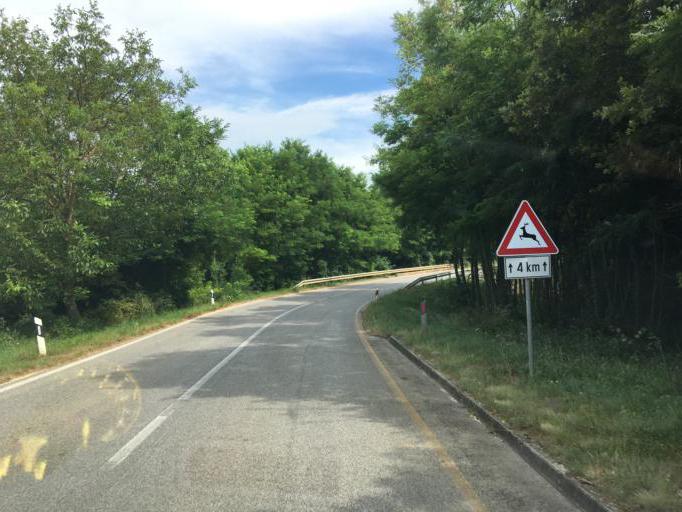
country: HR
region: Istarska
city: Karojba
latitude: 45.2859
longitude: 13.8340
